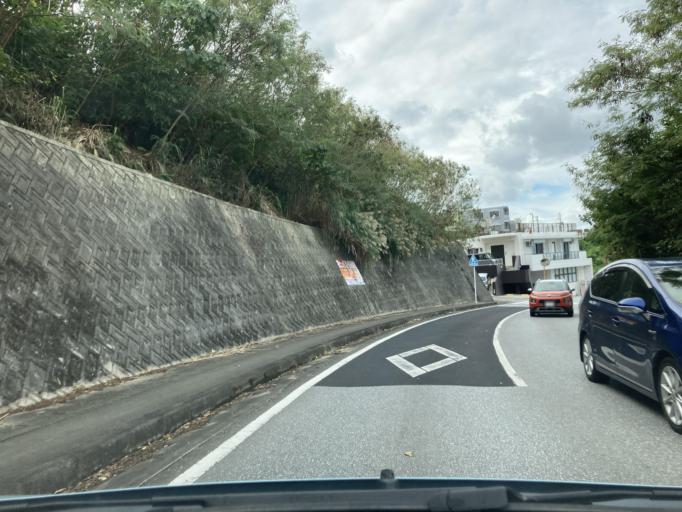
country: JP
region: Okinawa
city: Tomigusuku
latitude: 26.1606
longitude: 127.6761
